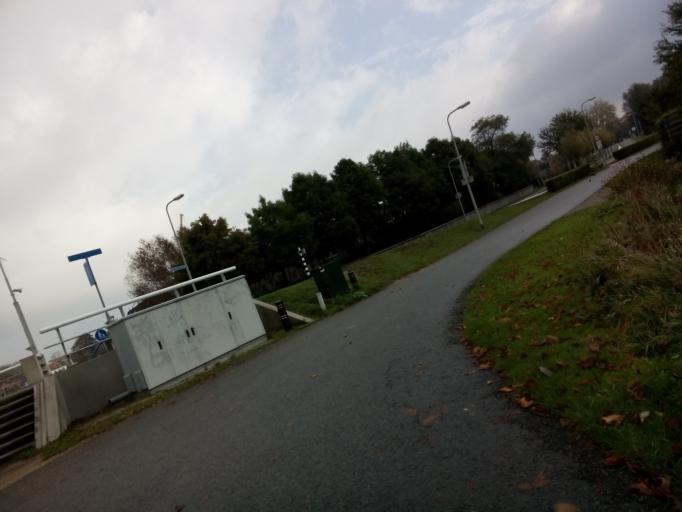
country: NL
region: South Holland
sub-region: Gemeente Delft
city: Delft
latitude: 51.9965
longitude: 4.3285
